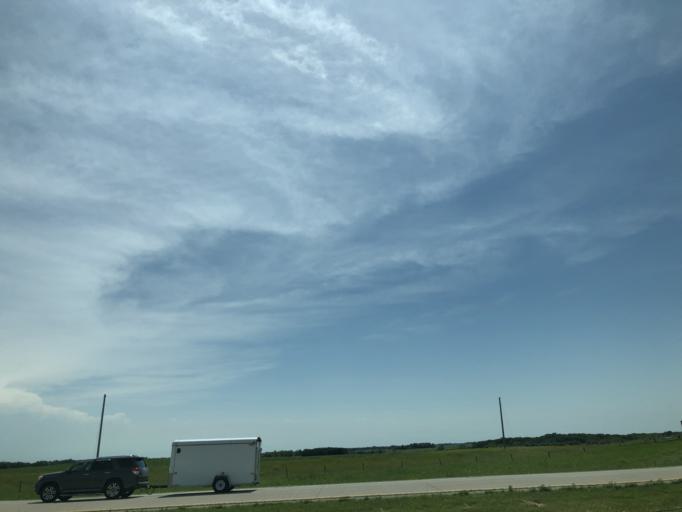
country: US
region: Minnesota
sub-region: Douglas County
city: Osakis
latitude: 45.8244
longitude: -95.1320
